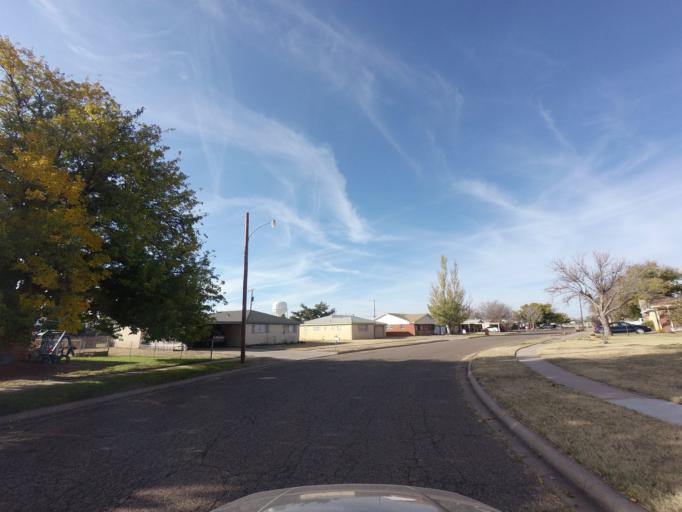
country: US
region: New Mexico
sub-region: Curry County
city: Clovis
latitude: 34.4248
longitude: -103.2243
